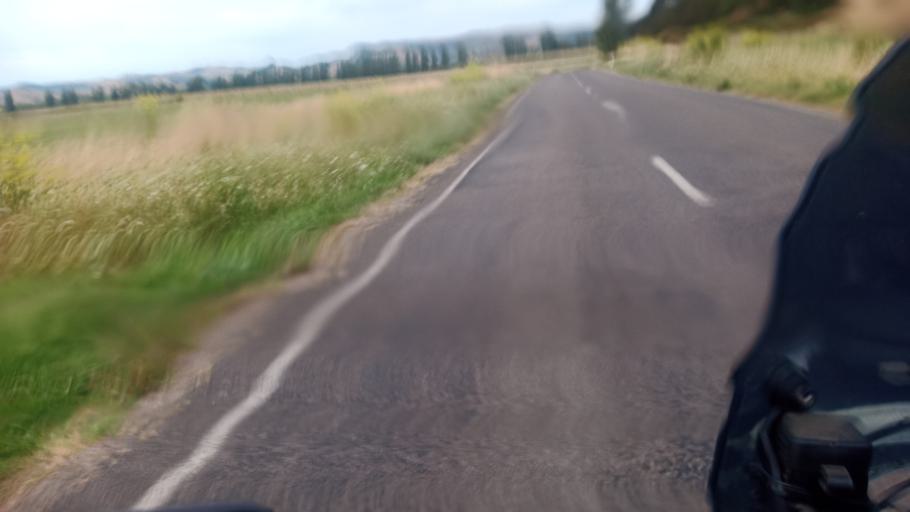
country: NZ
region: Gisborne
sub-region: Gisborne District
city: Gisborne
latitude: -38.5348
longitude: 177.8937
